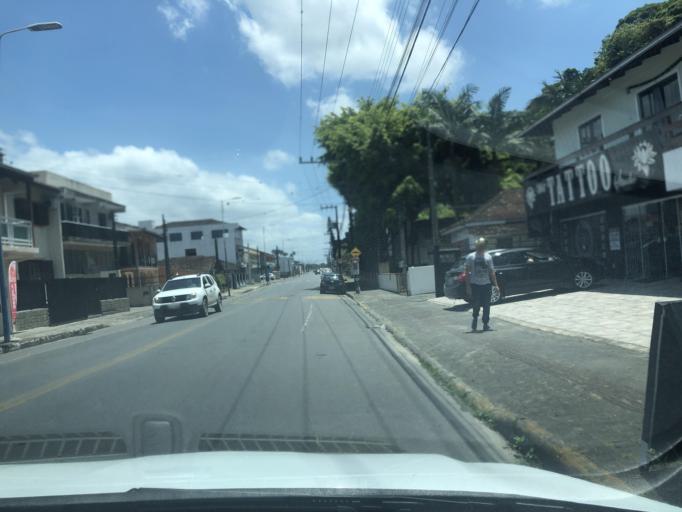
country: BR
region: Santa Catarina
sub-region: Sao Francisco Do Sul
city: Sao Francisco do Sul
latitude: -26.2460
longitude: -48.6344
